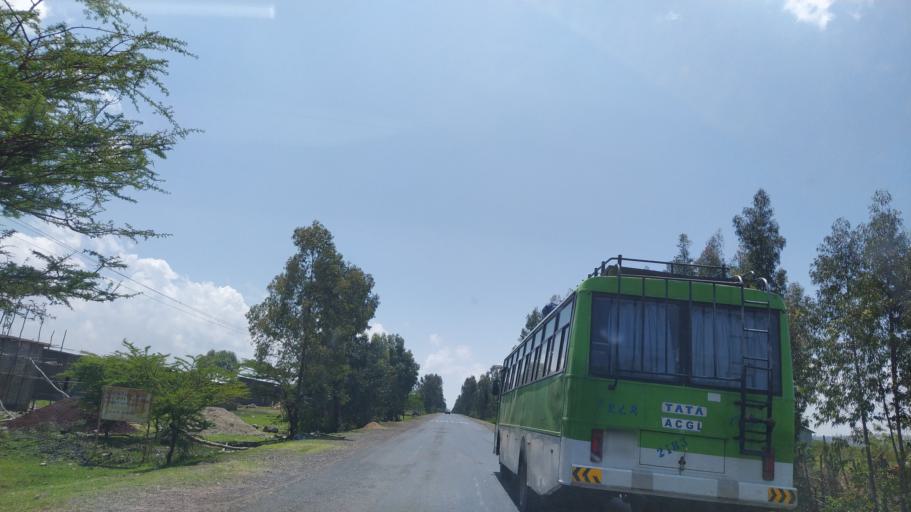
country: ET
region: Southern Nations, Nationalities, and People's Region
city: Butajira
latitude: 7.7855
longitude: 38.1422
